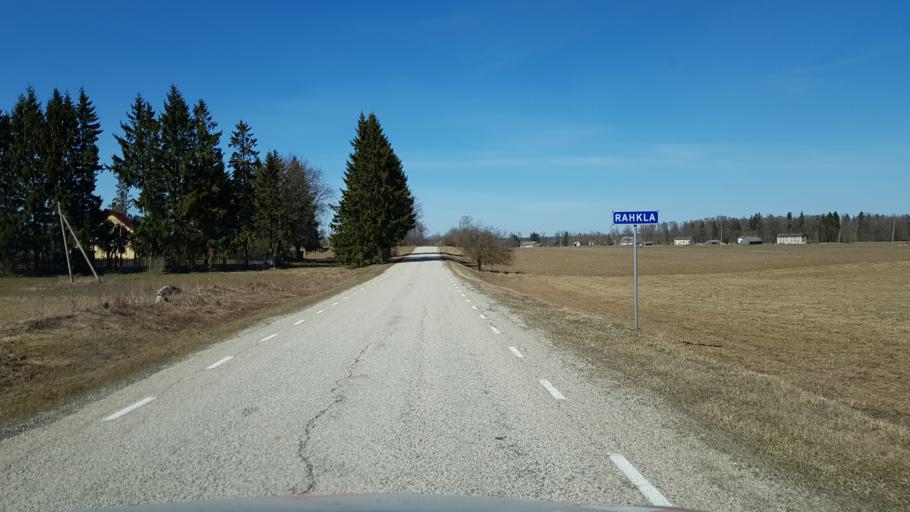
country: EE
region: Laeaene-Virumaa
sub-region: Vinni vald
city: Vinni
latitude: 59.0905
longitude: 26.5364
